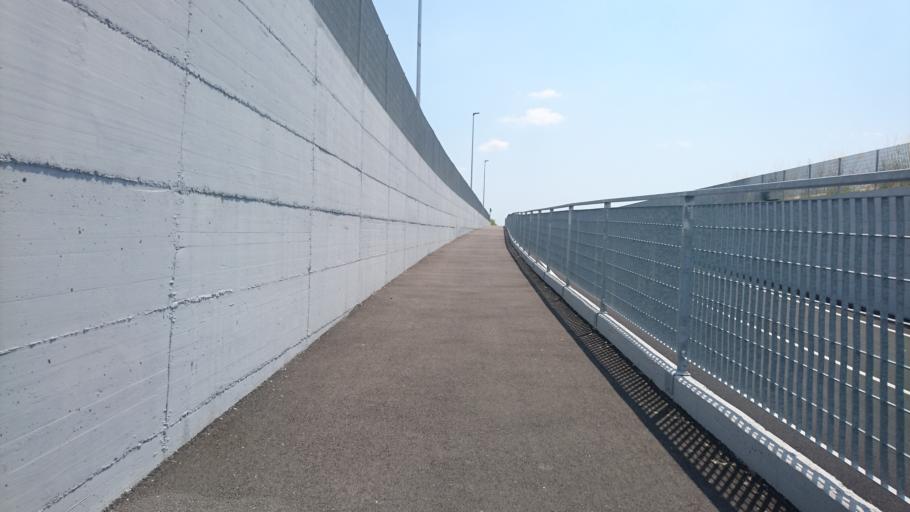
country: IT
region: Veneto
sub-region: Provincia di Padova
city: Monselice
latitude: 45.2165
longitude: 11.7266
